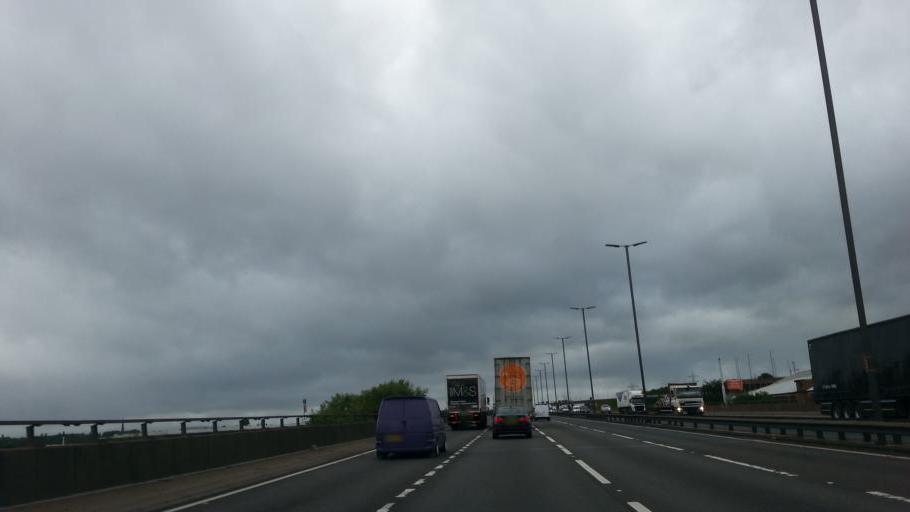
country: GB
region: England
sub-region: City and Borough of Birmingham
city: Birmingham
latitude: 52.5068
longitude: -1.8551
